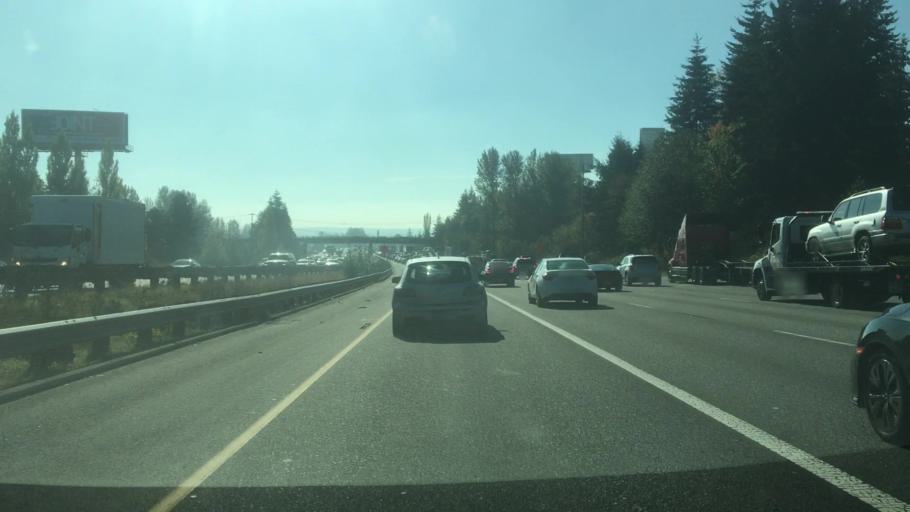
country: US
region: Washington
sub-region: Pierce County
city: Fife Heights
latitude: 47.2544
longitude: -122.3319
